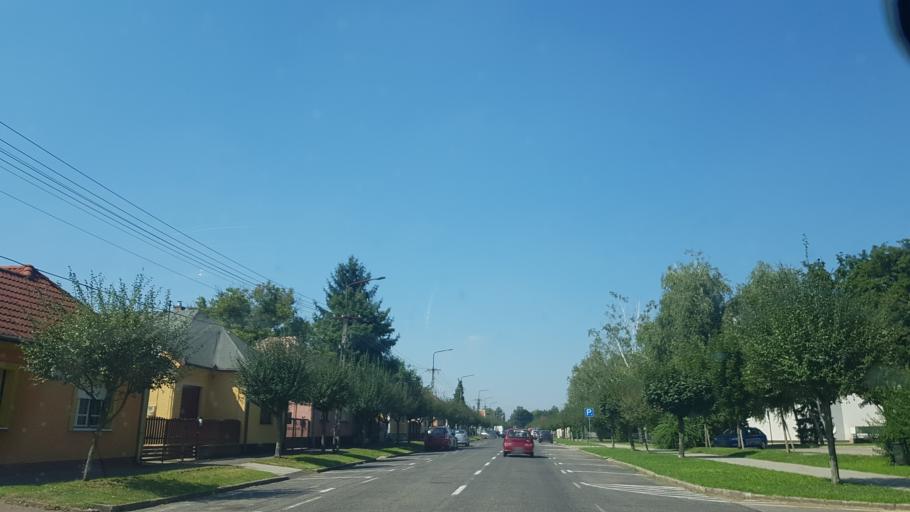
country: HU
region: Somogy
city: Nagyatad
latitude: 46.2326
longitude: 17.3610
